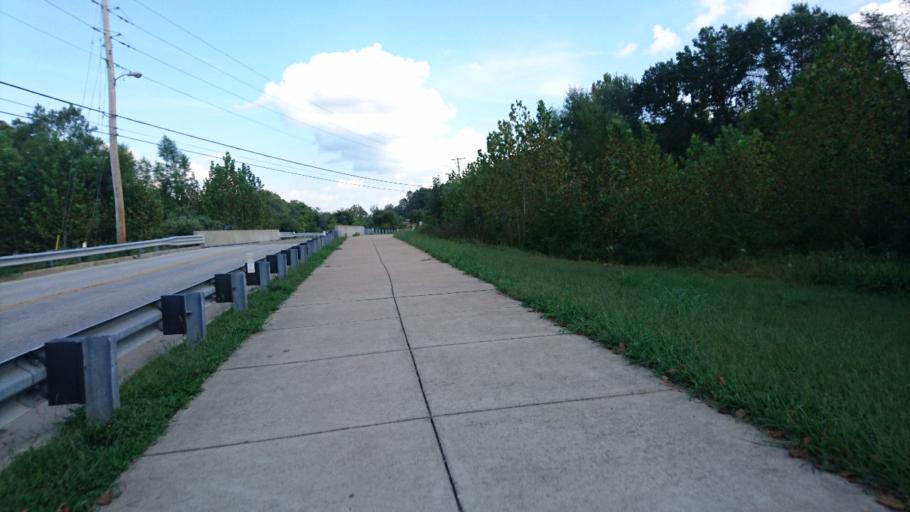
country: US
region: Missouri
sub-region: Saint Louis County
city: Eureka
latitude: 38.5166
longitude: -90.6384
